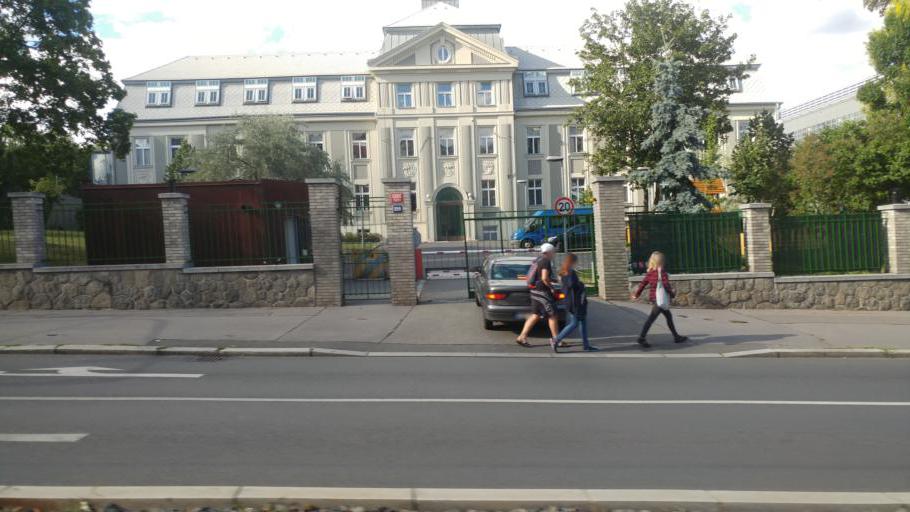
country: CZ
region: Praha
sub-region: Praha 8
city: Liben
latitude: 50.0780
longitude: 14.4769
